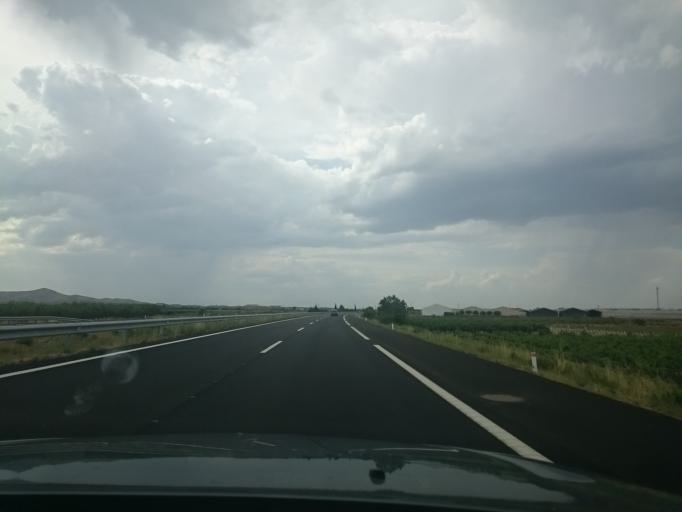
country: ES
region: La Rioja
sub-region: Provincia de La Rioja
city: Aldeanueva de Ebro
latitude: 42.2185
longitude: -1.8917
